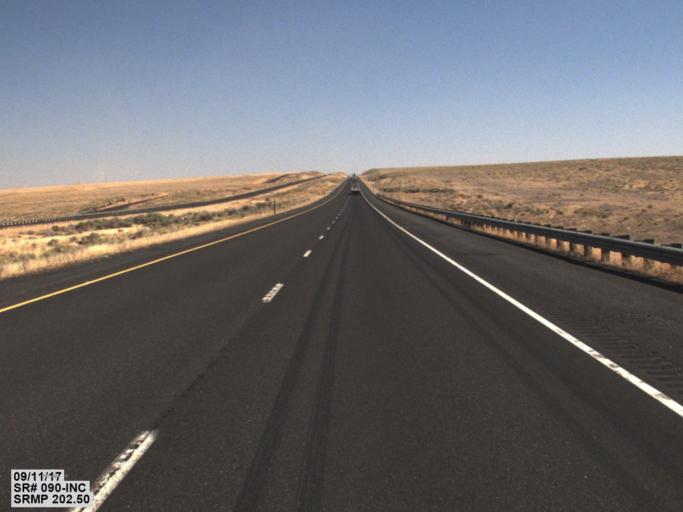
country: US
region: Washington
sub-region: Grant County
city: Warden
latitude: 47.0860
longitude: -118.7567
